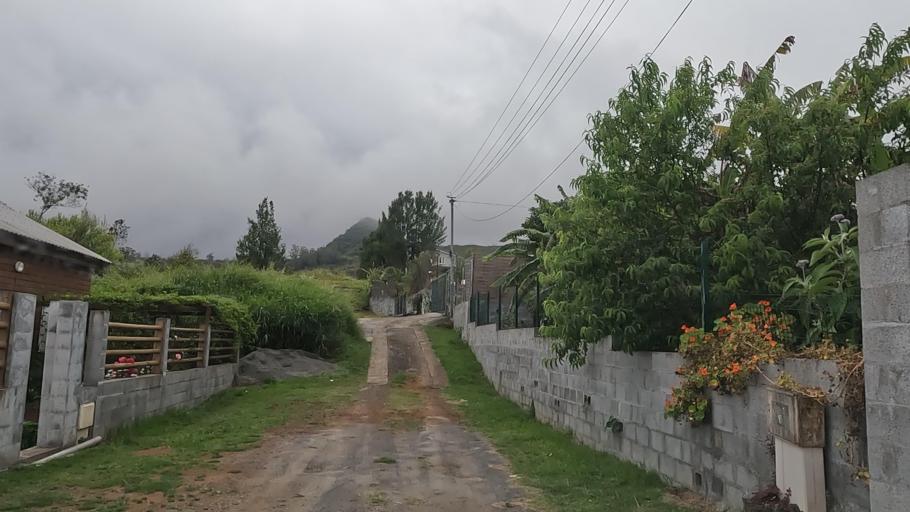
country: RE
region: Reunion
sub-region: Reunion
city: Salazie
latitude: -21.1517
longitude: 55.6186
